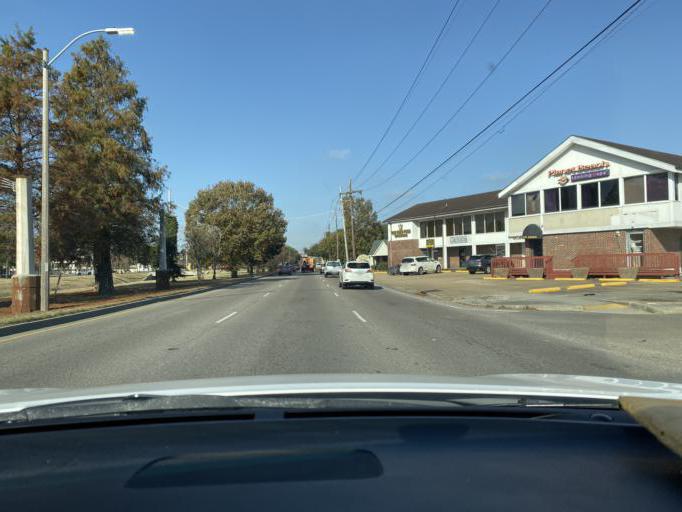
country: US
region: Louisiana
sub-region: Jefferson Parish
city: Terrytown
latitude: 29.9220
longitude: -90.0154
